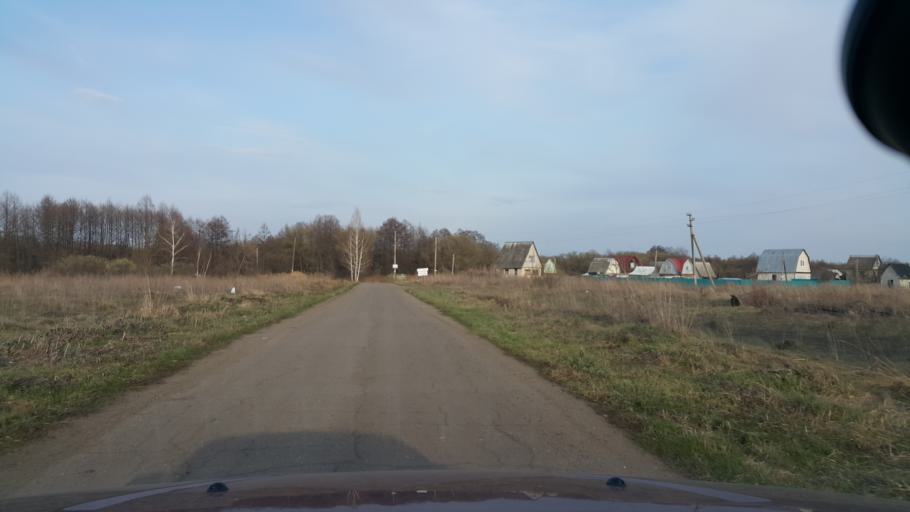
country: RU
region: Tambov
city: Kotovsk
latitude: 52.5899
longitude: 41.4604
